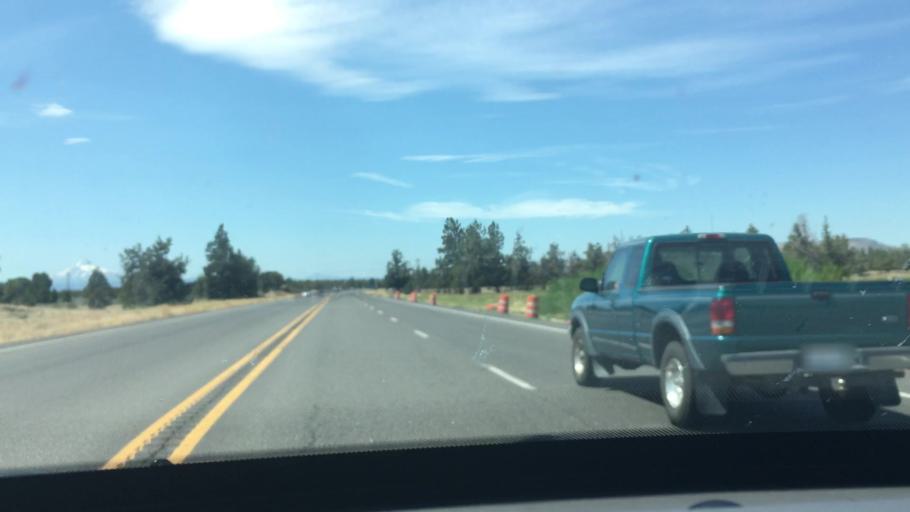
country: US
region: Oregon
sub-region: Deschutes County
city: Terrebonne
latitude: 44.3835
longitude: -121.1823
